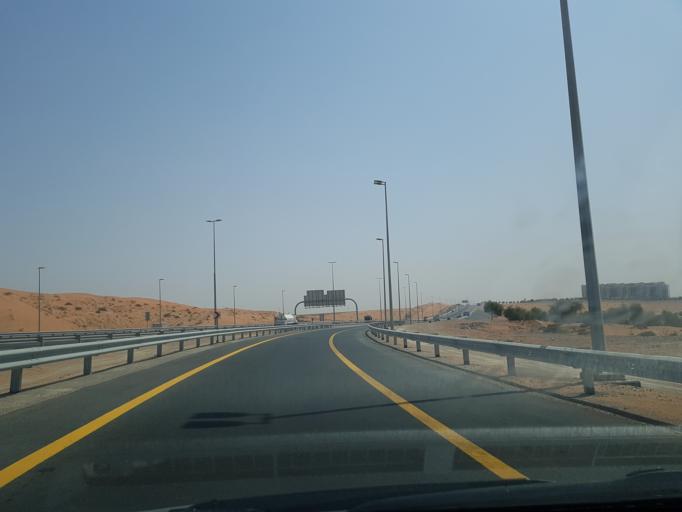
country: AE
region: Ra's al Khaymah
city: Ras al-Khaimah
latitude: 25.6348
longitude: 55.8358
